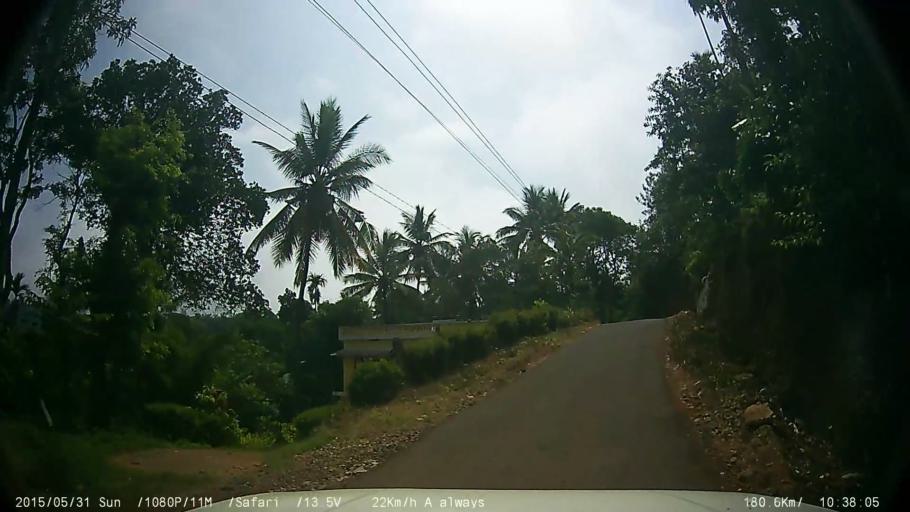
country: IN
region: Kerala
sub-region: Wayanad
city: Kalpetta
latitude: 11.5092
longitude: 76.1521
